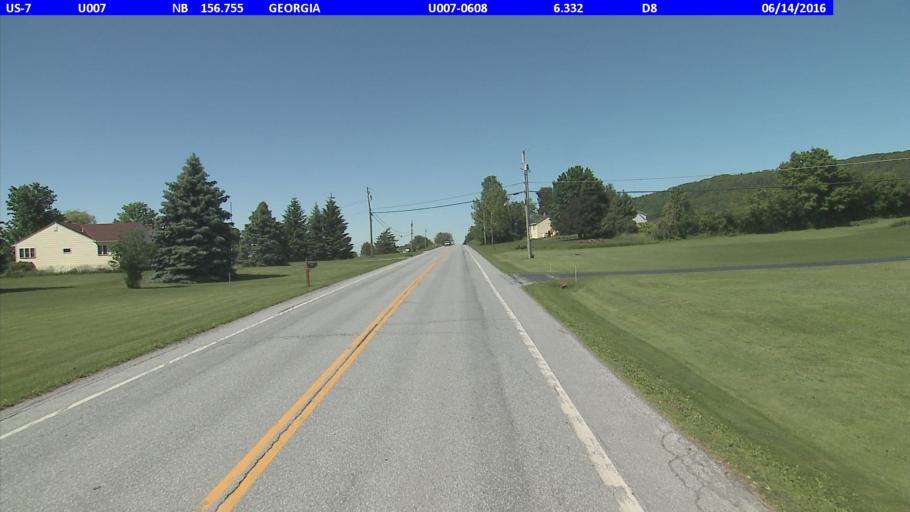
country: US
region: Vermont
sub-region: Franklin County
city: Saint Albans
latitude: 44.7622
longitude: -73.1095
